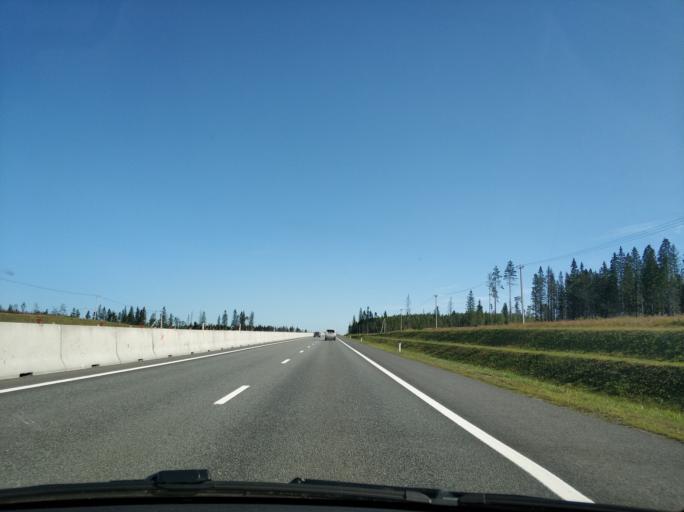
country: RU
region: Leningrad
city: Sosnovo
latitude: 60.4828
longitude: 30.1958
